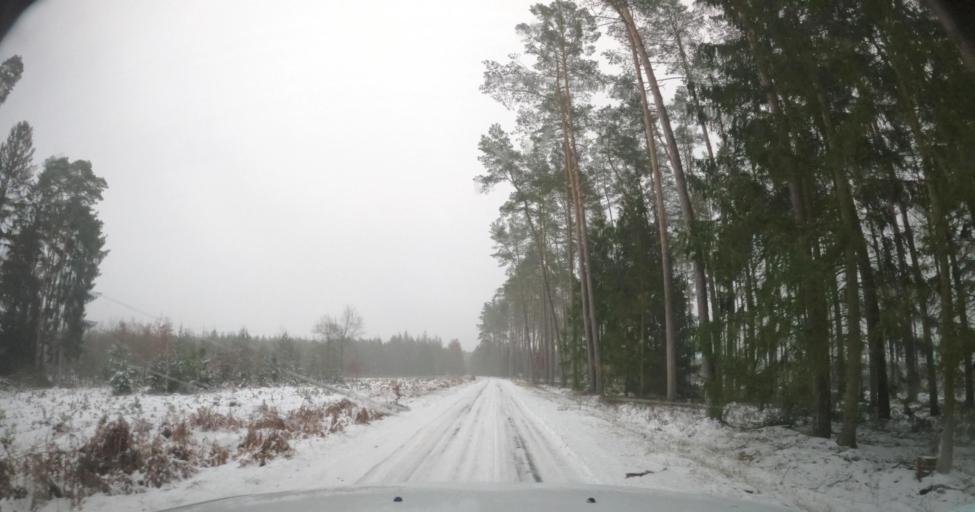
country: PL
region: West Pomeranian Voivodeship
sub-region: Powiat goleniowski
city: Przybiernow
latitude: 53.6608
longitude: 14.7915
